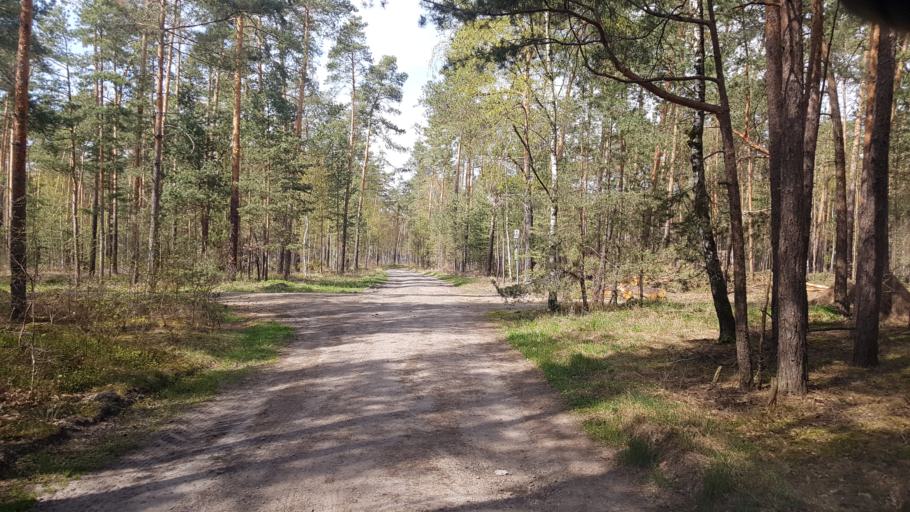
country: DE
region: Brandenburg
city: Plessa
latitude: 51.5438
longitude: 13.6598
